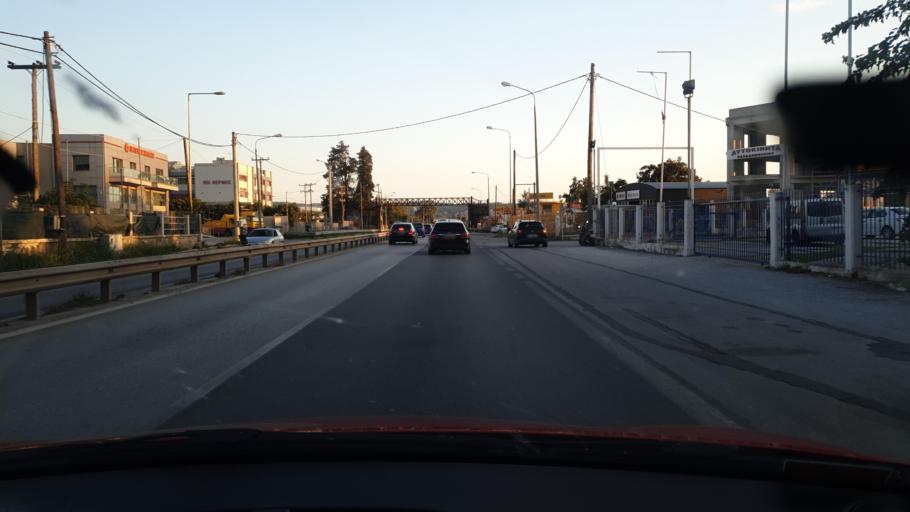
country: GR
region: Central Macedonia
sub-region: Nomos Thessalonikis
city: Neo Rysi
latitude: 40.5251
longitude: 22.9947
